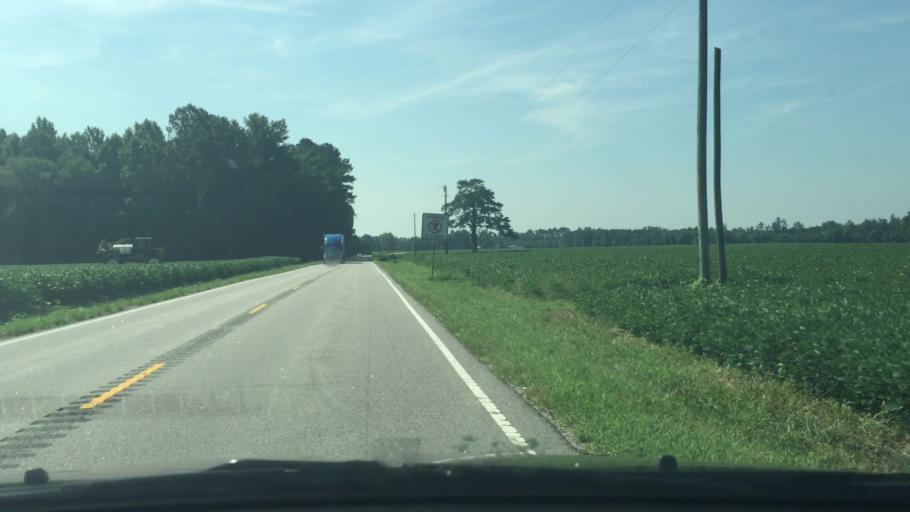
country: US
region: Virginia
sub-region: Southampton County
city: Courtland
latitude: 36.8508
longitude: -77.1338
